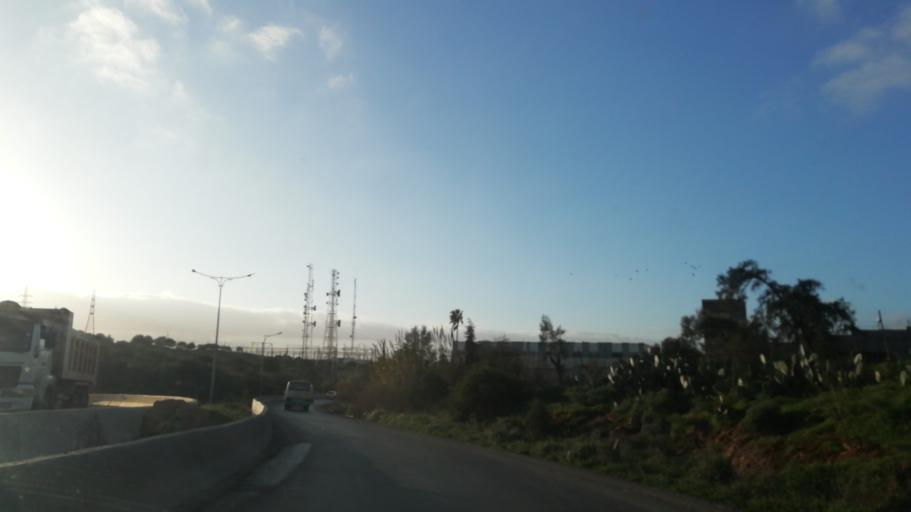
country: DZ
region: Oran
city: Oran
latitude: 35.6433
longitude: -0.7108
